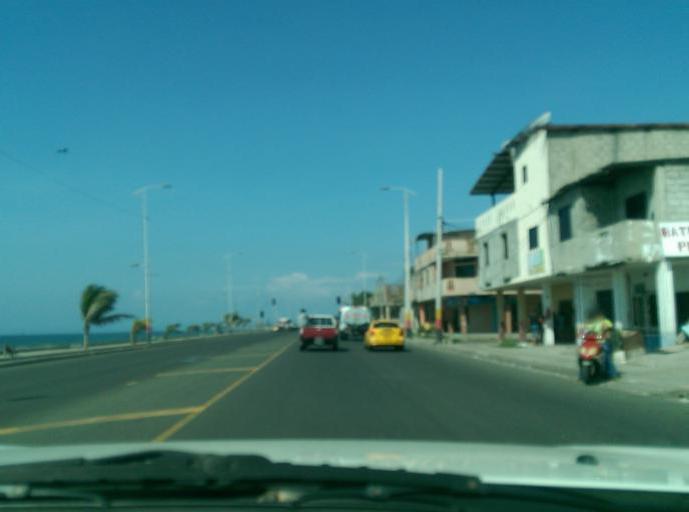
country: EC
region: Manabi
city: Manta
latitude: -0.9496
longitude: -80.7040
